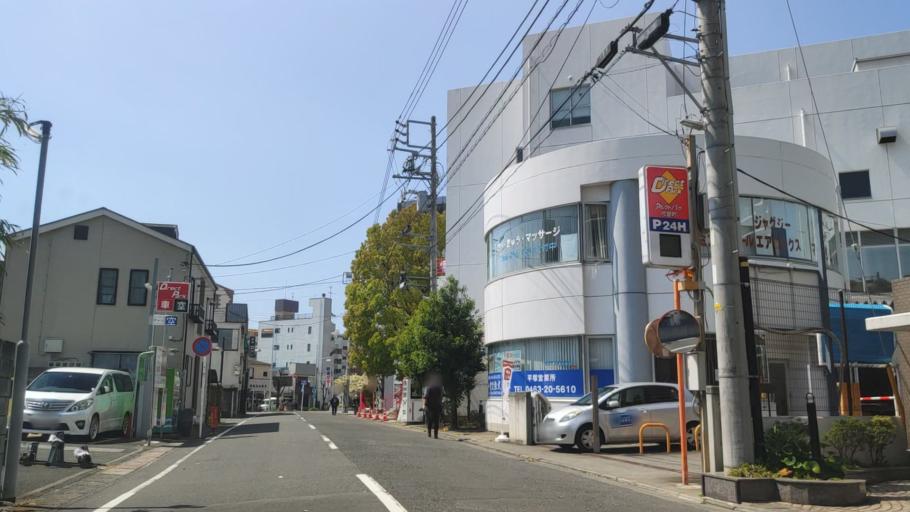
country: JP
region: Kanagawa
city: Hiratsuka
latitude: 35.3281
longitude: 139.3545
